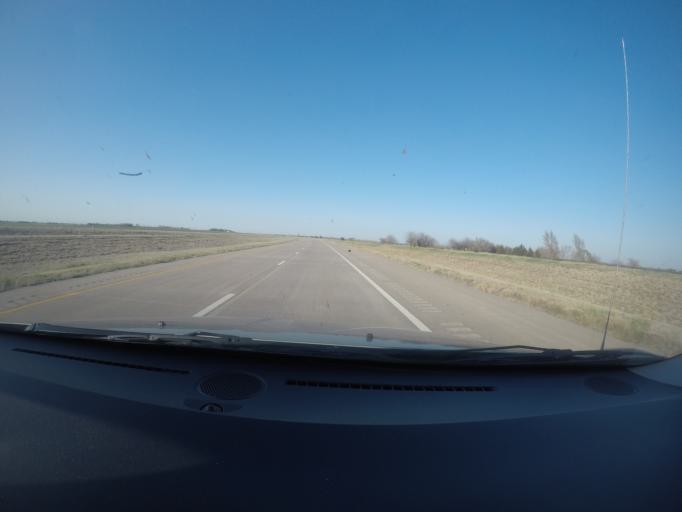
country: US
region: Kansas
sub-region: McPherson County
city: Inman
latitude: 38.2962
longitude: -97.7275
